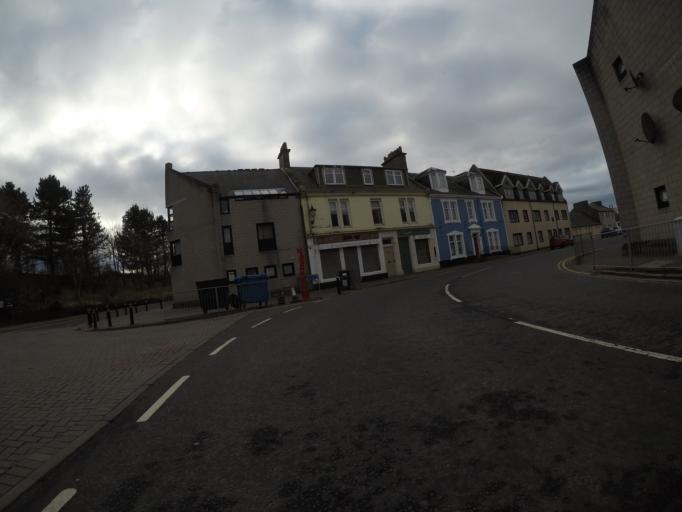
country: GB
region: Scotland
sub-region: North Ayrshire
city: Irvine
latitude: 55.6114
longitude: -4.6758
